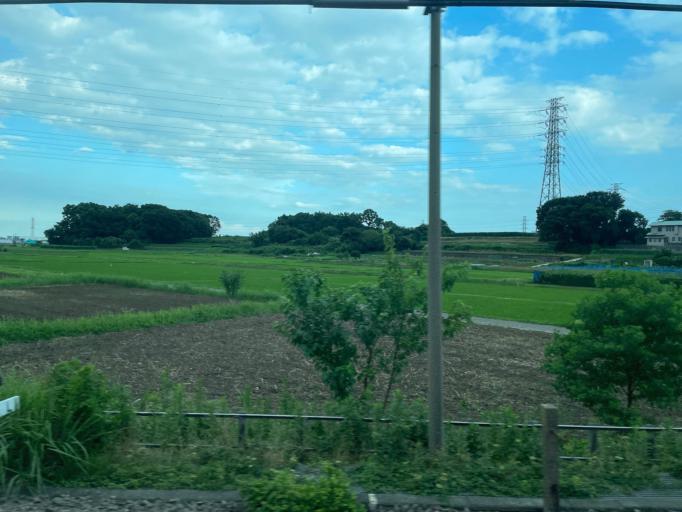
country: JP
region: Kanagawa
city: Isehara
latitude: 35.4018
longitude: 139.3229
